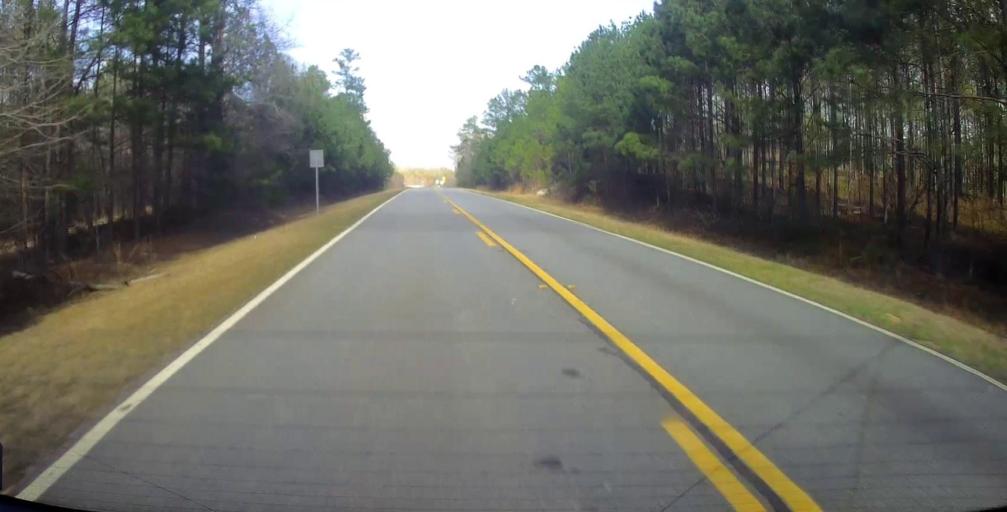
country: US
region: Georgia
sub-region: Twiggs County
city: Jeffersonville
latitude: 32.7674
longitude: -83.3377
